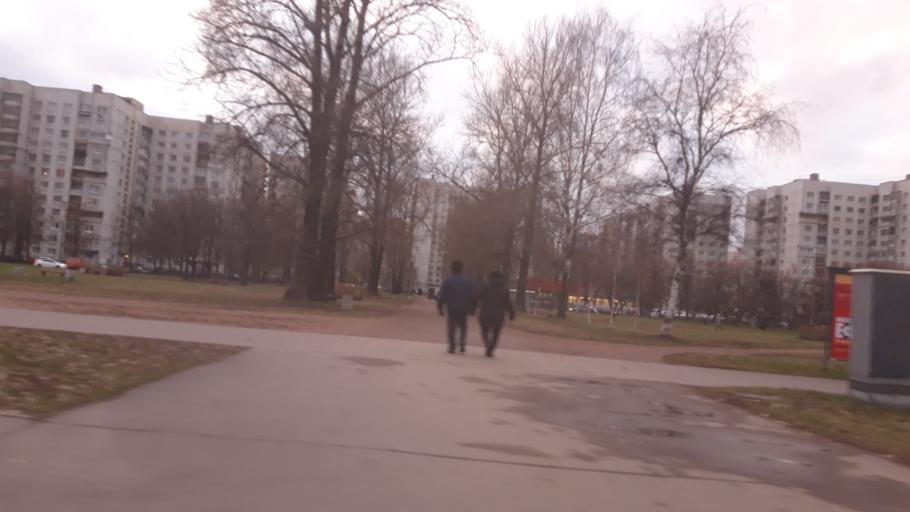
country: RU
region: St.-Petersburg
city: Kupchino
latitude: 59.8347
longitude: 30.3218
